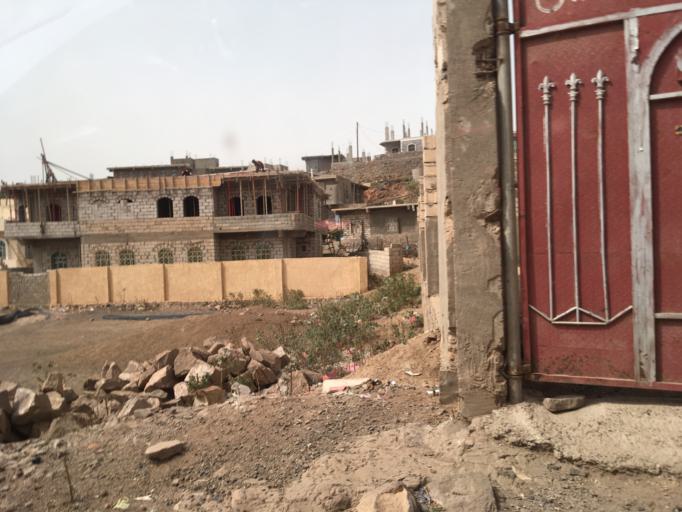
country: YE
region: Ad Dali'
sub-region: Ad Dhale'e
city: Dhalie
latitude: 13.7080
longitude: 44.7370
